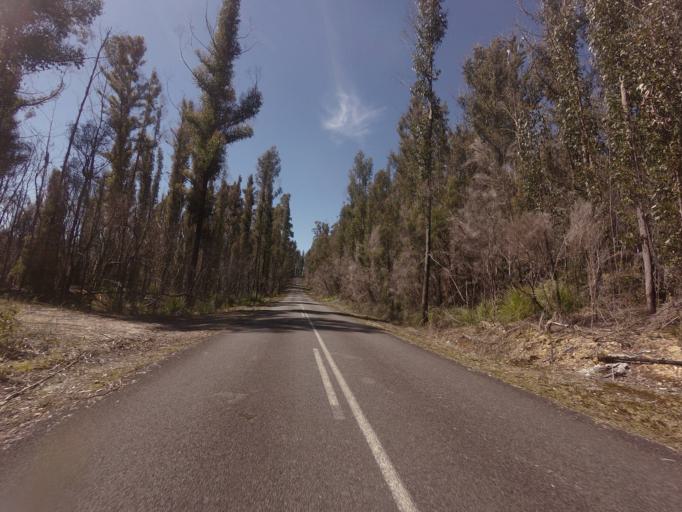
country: AU
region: Tasmania
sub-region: Huon Valley
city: Geeveston
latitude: -42.8430
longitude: 146.2521
